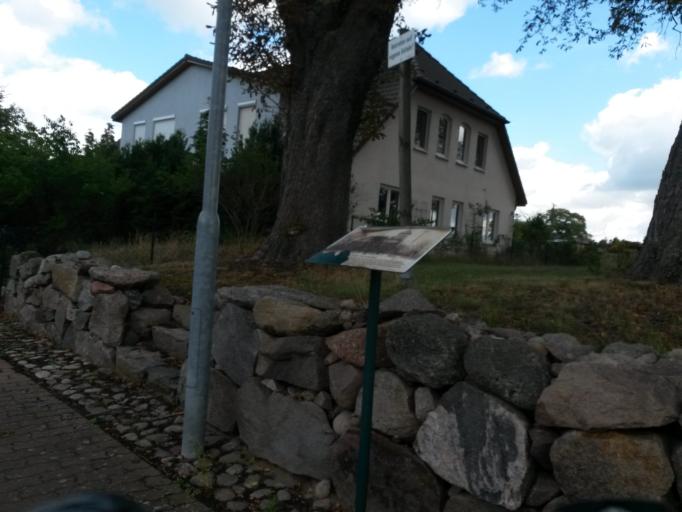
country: DE
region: Brandenburg
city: Milmersdorf
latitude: 53.0885
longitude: 13.6014
